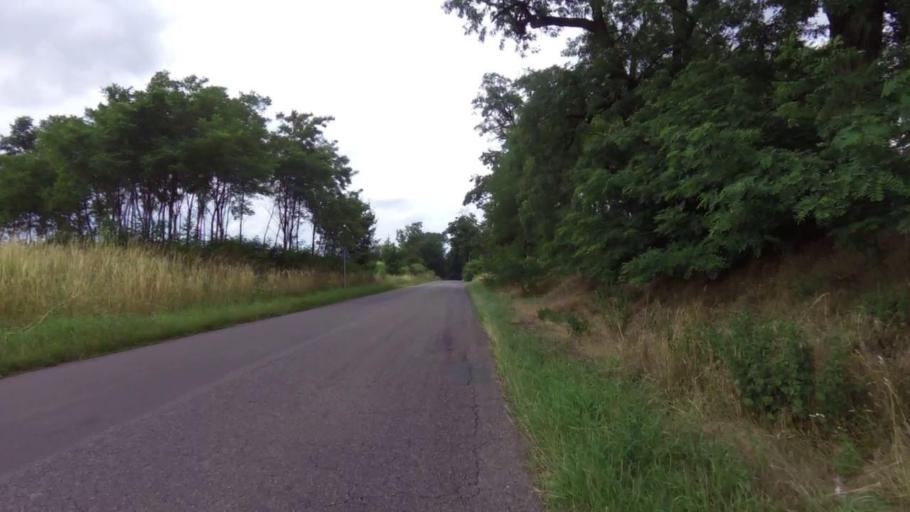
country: PL
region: West Pomeranian Voivodeship
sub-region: Powiat gryfinski
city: Moryn
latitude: 52.8647
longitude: 14.3855
